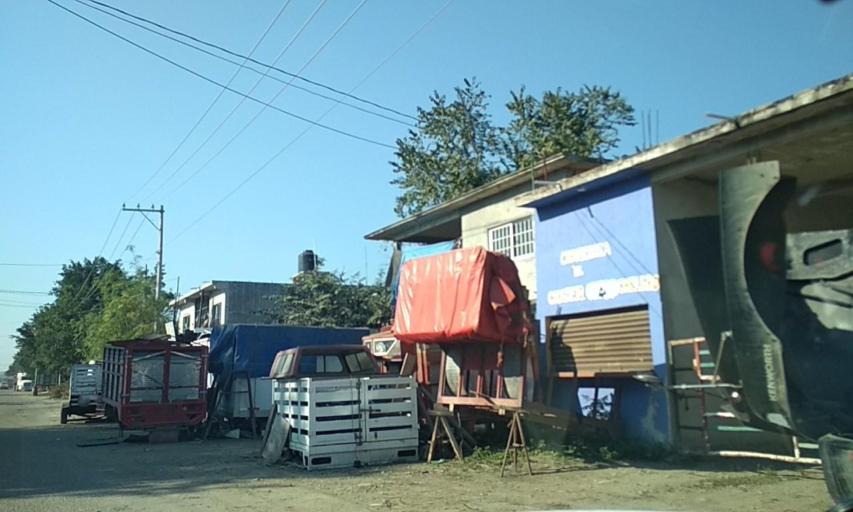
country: MX
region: Veracruz
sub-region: Papantla
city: El Chote
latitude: 20.4050
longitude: -97.3429
